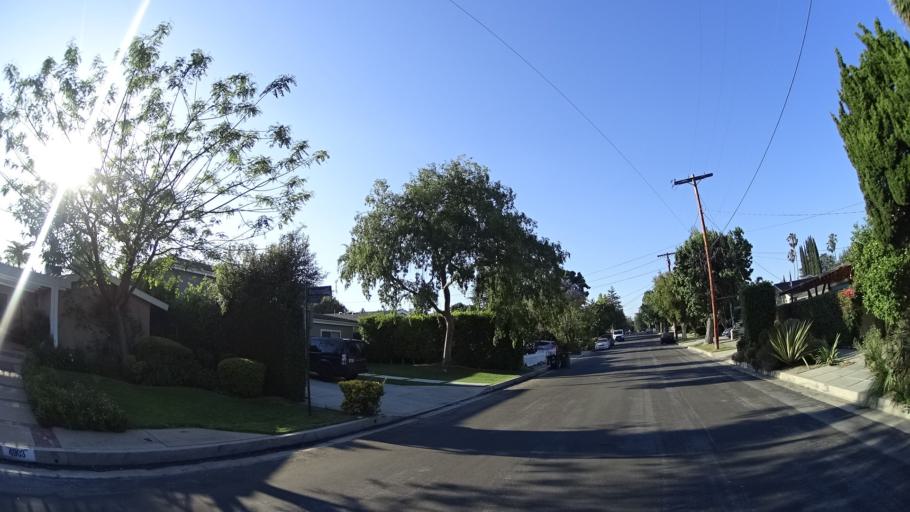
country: US
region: California
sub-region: Los Angeles County
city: North Hollywood
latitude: 34.1596
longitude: -118.4094
